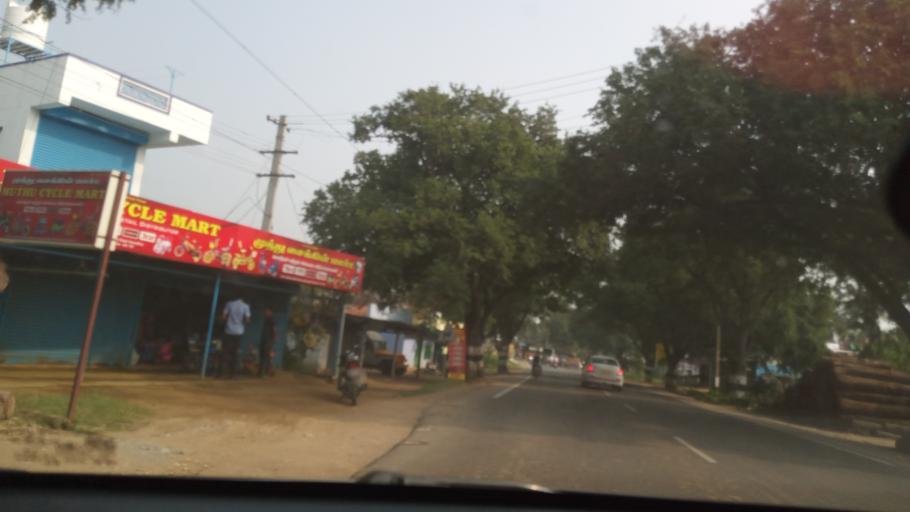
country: IN
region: Tamil Nadu
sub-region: Coimbatore
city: Periyanayakkanpalaiyam
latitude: 11.1486
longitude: 77.0449
